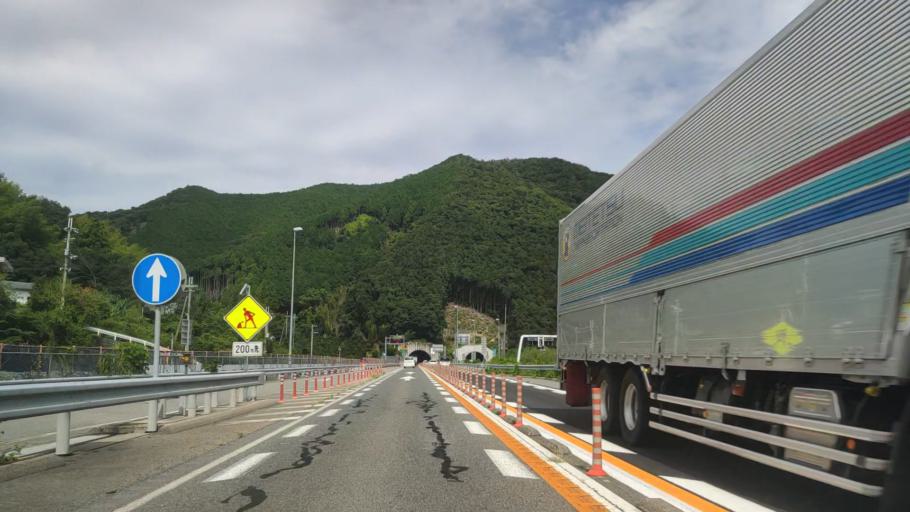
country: JP
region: Wakayama
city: Gobo
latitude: 33.9690
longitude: 135.1973
